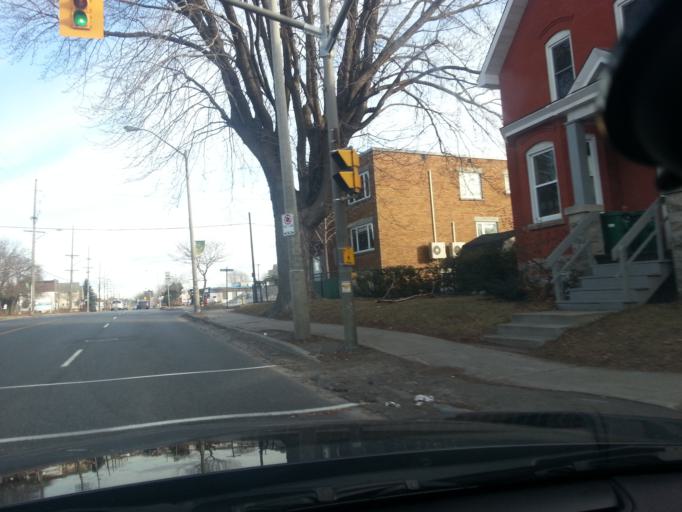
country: CA
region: Ontario
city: Ottawa
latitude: 45.4313
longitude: -75.6605
